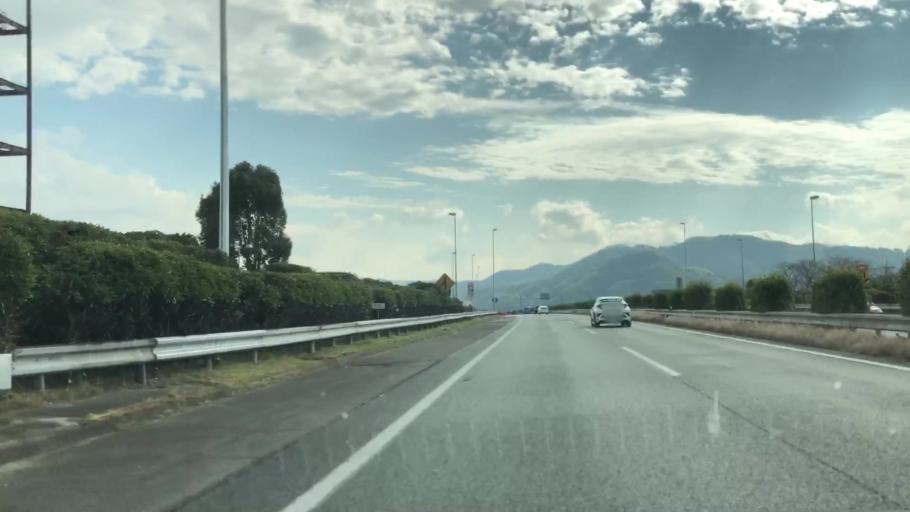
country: JP
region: Fukuoka
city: Setakamachi-takayanagi
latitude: 33.1282
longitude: 130.5178
